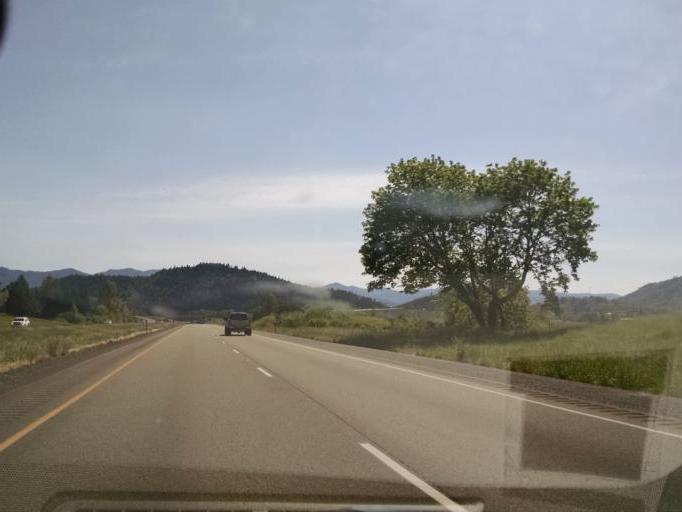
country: US
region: Oregon
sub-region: Douglas County
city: Tri-City
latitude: 42.9828
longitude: -123.3324
